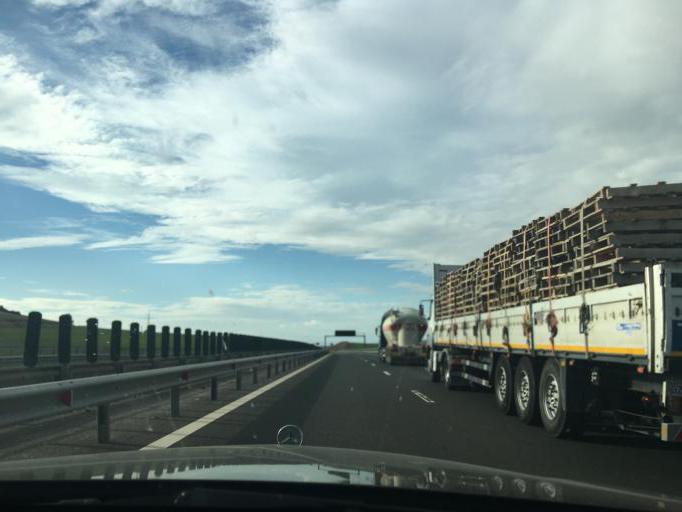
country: RO
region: Alba
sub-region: Comuna Garbova
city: Garbova
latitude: 45.9138
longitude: 23.7334
